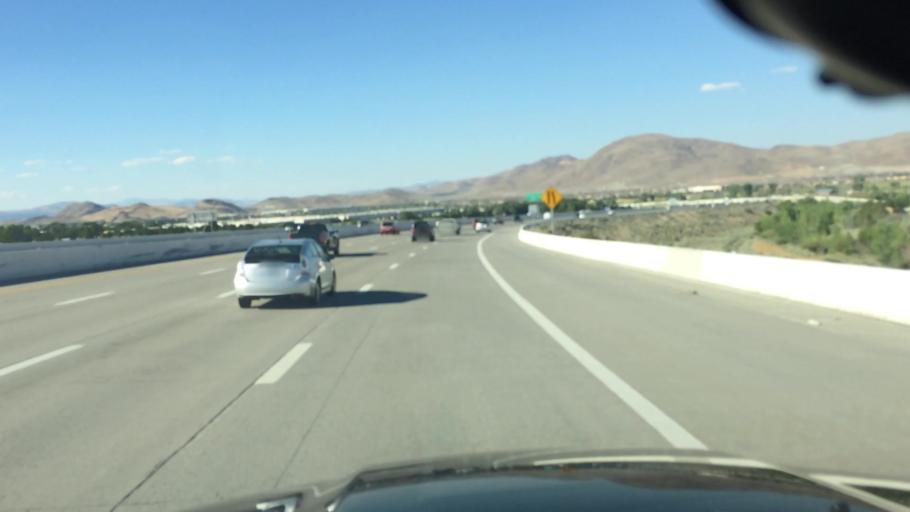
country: US
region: Nevada
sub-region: Washoe County
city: Sparks
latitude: 39.4039
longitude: -119.7549
